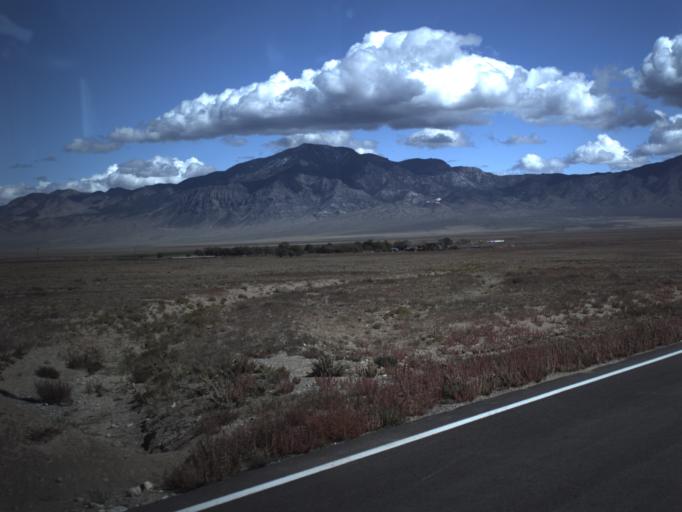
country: US
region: Utah
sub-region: Beaver County
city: Milford
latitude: 38.4829
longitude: -113.4452
